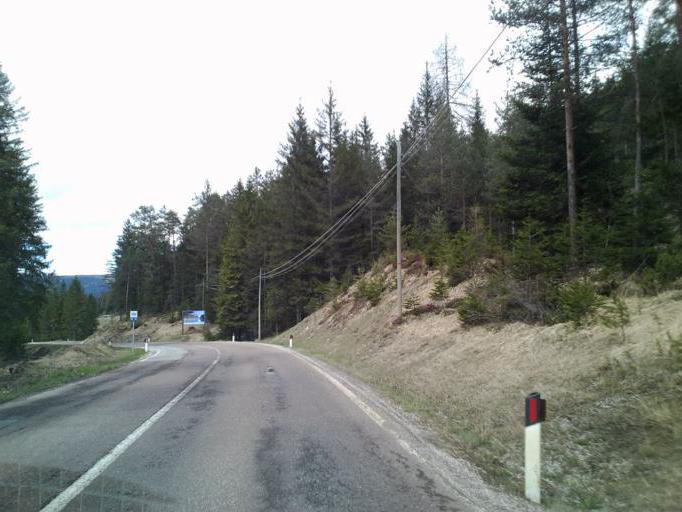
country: IT
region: Trentino-Alto Adige
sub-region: Bolzano
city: Dobbiaco
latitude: 46.7008
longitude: 12.2227
